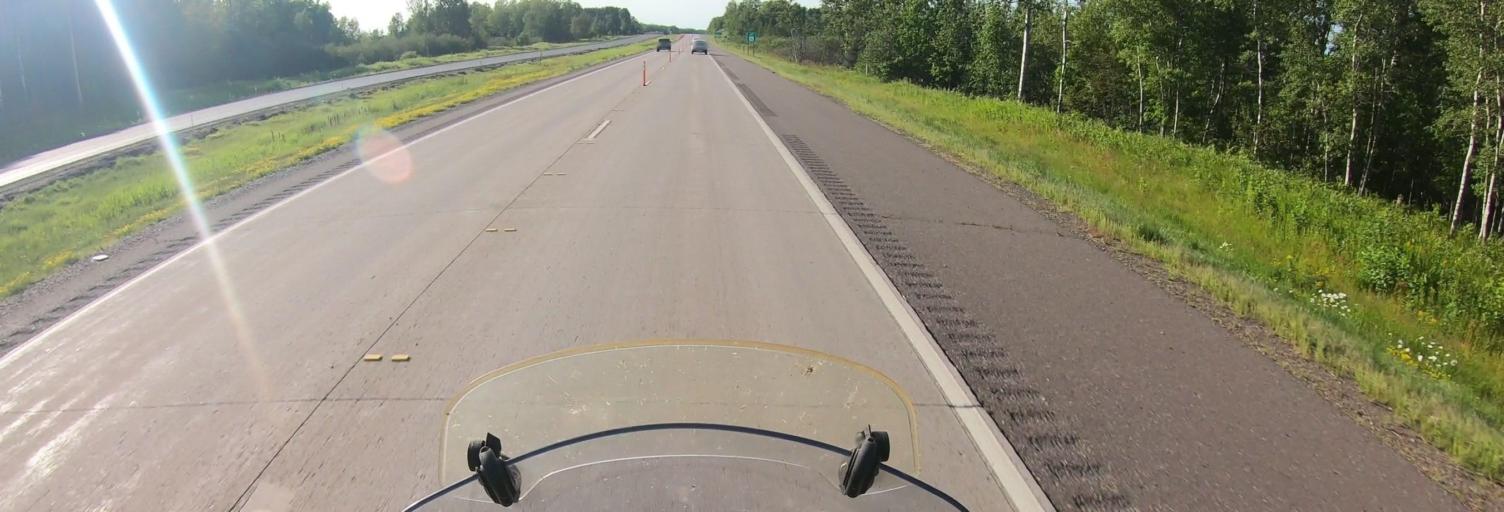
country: US
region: Minnesota
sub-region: Saint Louis County
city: Hermantown
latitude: 46.9064
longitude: -92.3835
